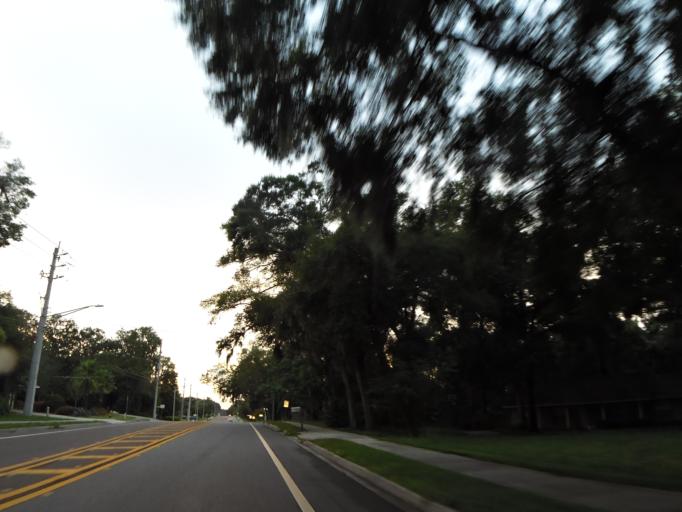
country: US
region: Florida
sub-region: Duval County
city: Jacksonville
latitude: 30.3590
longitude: -81.5497
